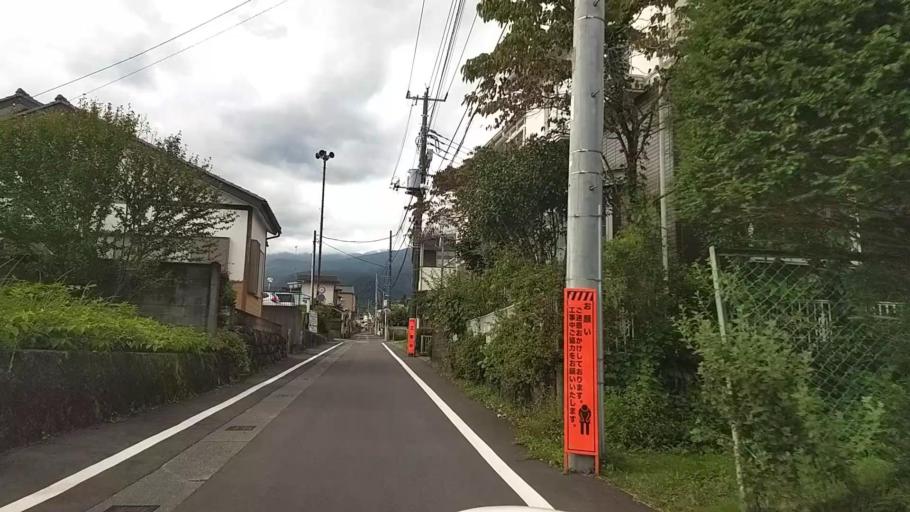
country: JP
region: Tochigi
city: Nikko
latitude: 36.7498
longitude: 139.6184
